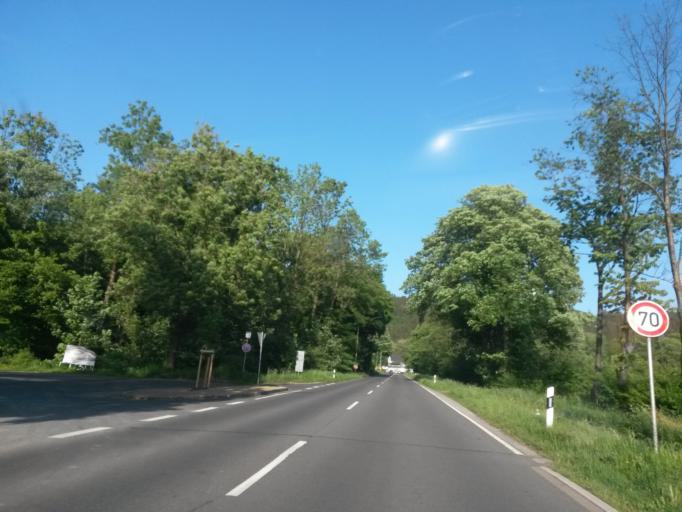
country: DE
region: North Rhine-Westphalia
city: Bergneustadt
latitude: 51.0226
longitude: 7.6760
